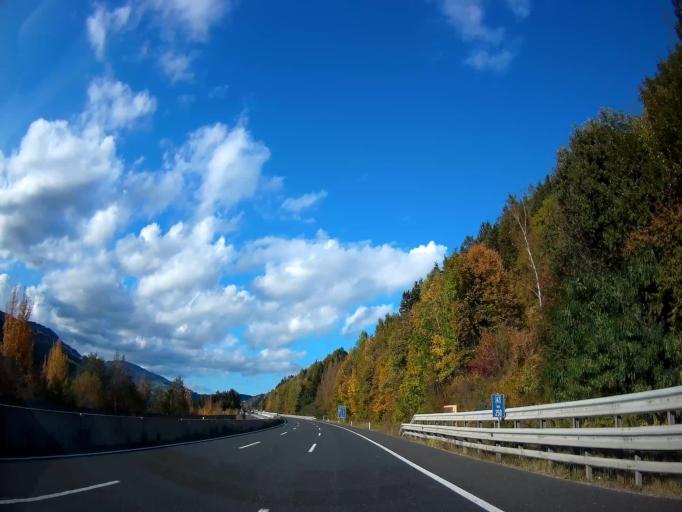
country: AT
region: Carinthia
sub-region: Politischer Bezirk Wolfsberg
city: Wolfsberg
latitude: 46.8676
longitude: 14.8363
